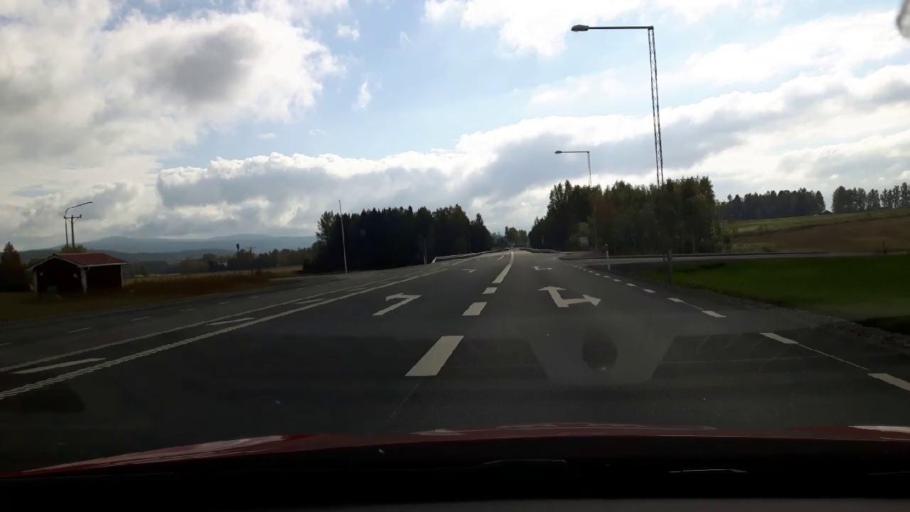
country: SE
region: Gaevleborg
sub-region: Bollnas Kommun
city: Arbra
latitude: 61.5413
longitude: 16.3573
